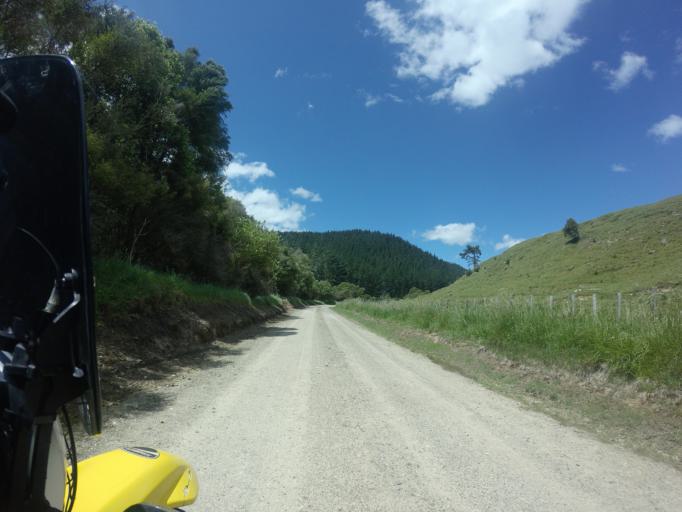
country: NZ
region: Hawke's Bay
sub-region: Wairoa District
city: Wairoa
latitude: -38.9657
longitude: 177.6658
